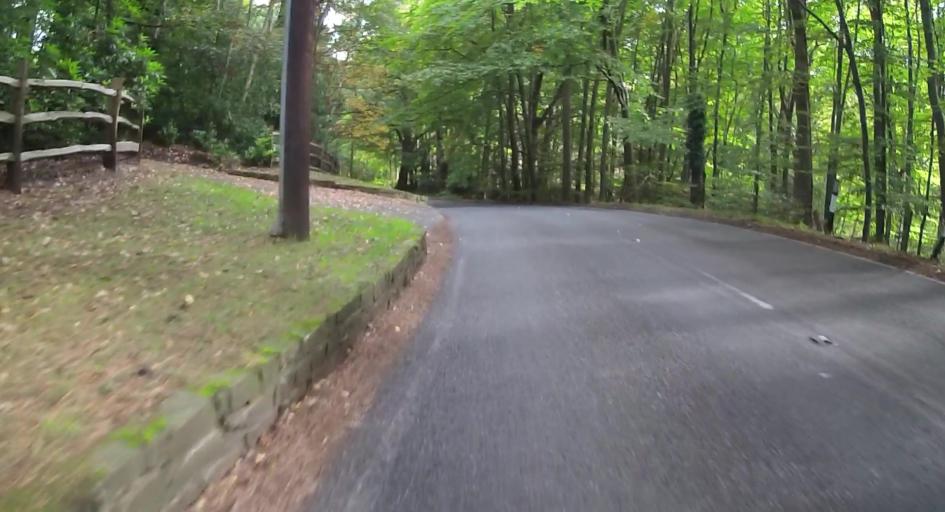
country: GB
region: England
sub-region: Surrey
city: Seale
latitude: 51.2060
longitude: -0.7483
